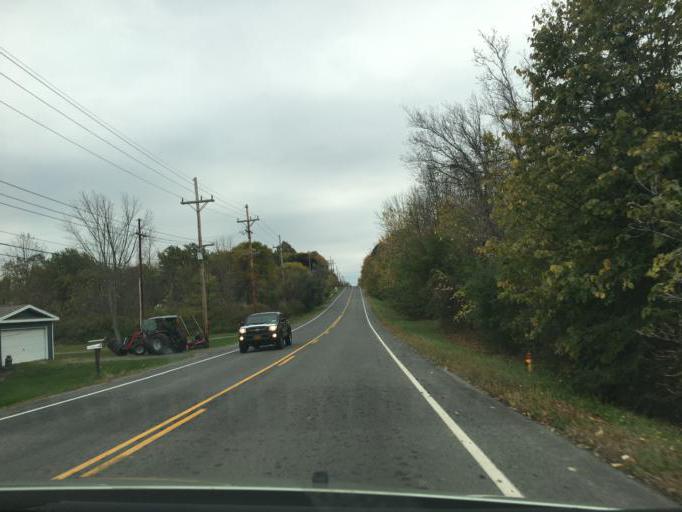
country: US
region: New York
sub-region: Ontario County
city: Canandaigua
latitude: 42.9362
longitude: -77.3150
